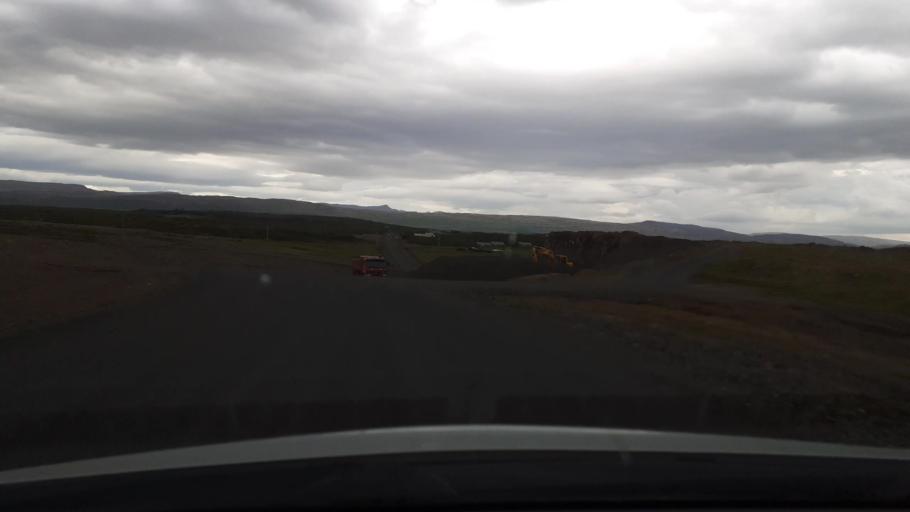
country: IS
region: West
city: Borgarnes
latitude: 64.6684
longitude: -21.6986
